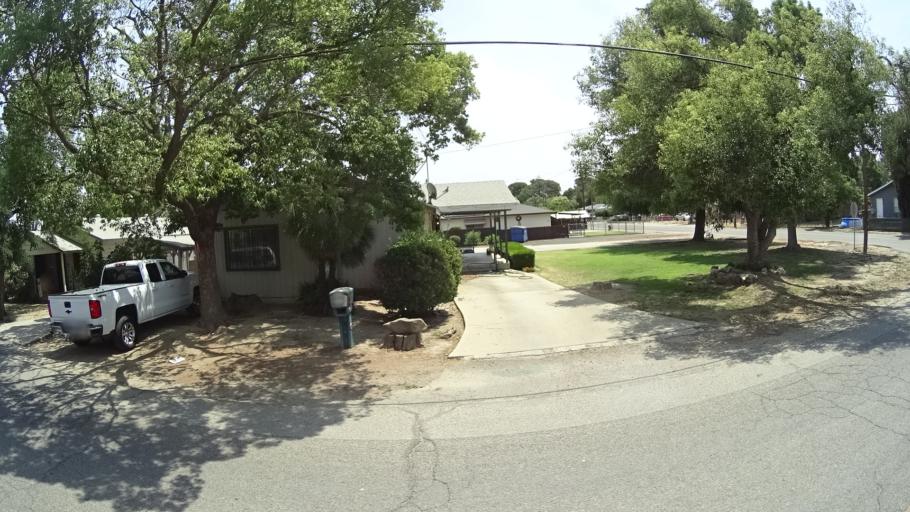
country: US
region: California
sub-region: Fresno County
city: West Park
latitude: 36.7540
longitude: -119.8532
